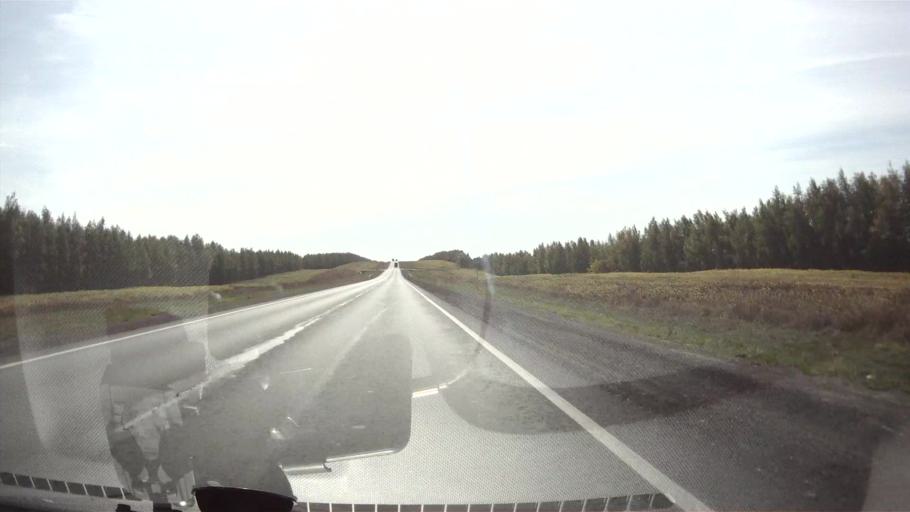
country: RU
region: Samara
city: Syzran'
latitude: 52.9183
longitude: 48.3018
